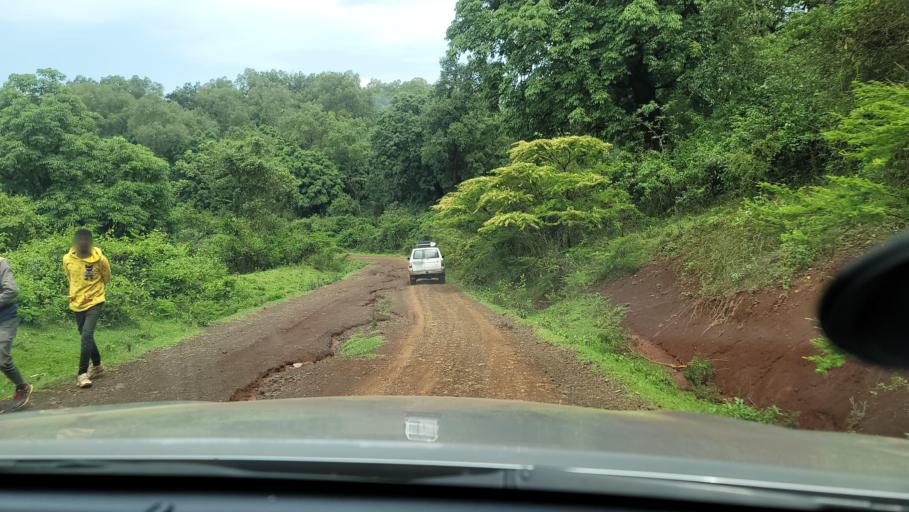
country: ET
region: Oromiya
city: Agaro
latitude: 7.7120
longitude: 36.2556
